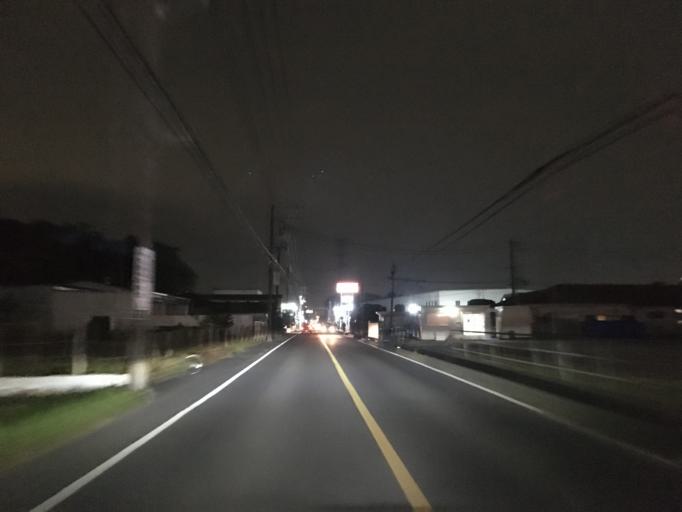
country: JP
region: Saitama
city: Sayama
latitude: 35.8255
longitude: 139.4368
